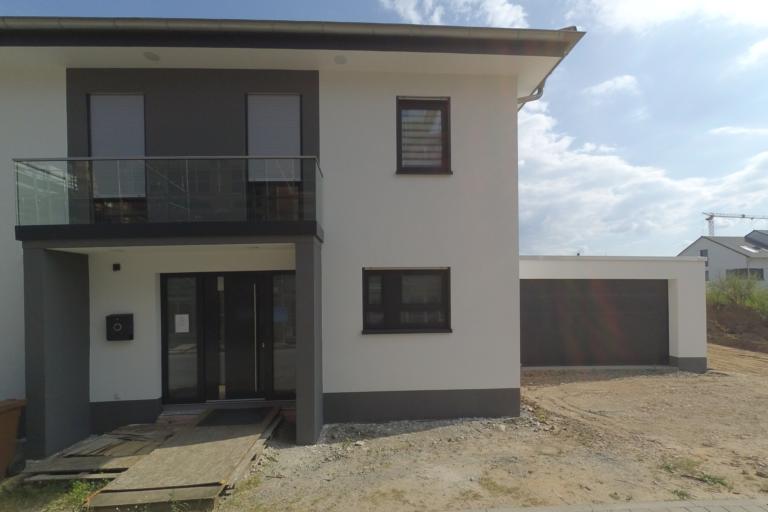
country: DE
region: Hesse
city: Viernheim
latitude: 49.5391
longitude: 8.5630
